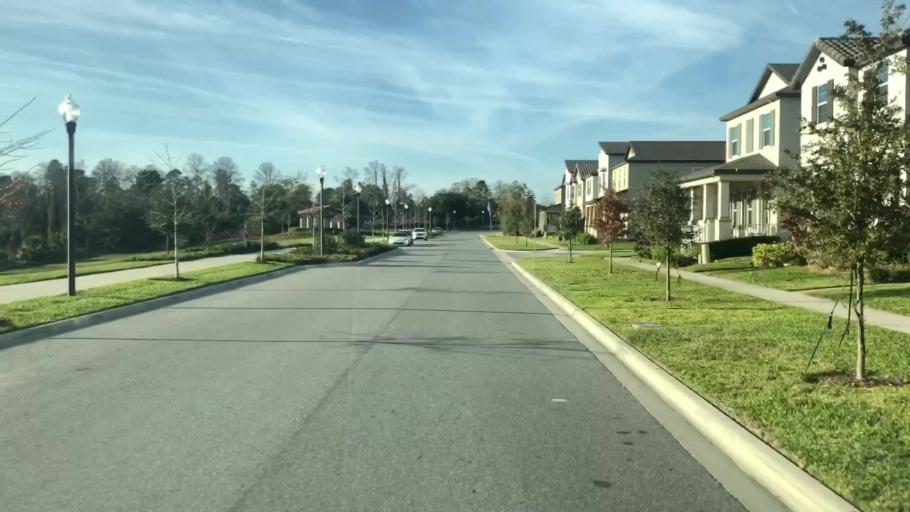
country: US
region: Florida
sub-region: Polk County
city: Citrus Ridge
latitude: 28.4285
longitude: -81.6225
